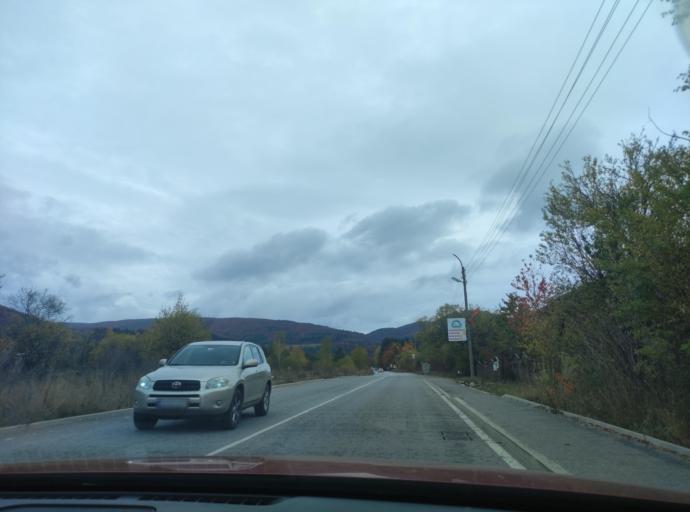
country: BG
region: Sofiya
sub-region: Obshtina Godech
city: Godech
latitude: 43.0964
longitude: 23.1002
